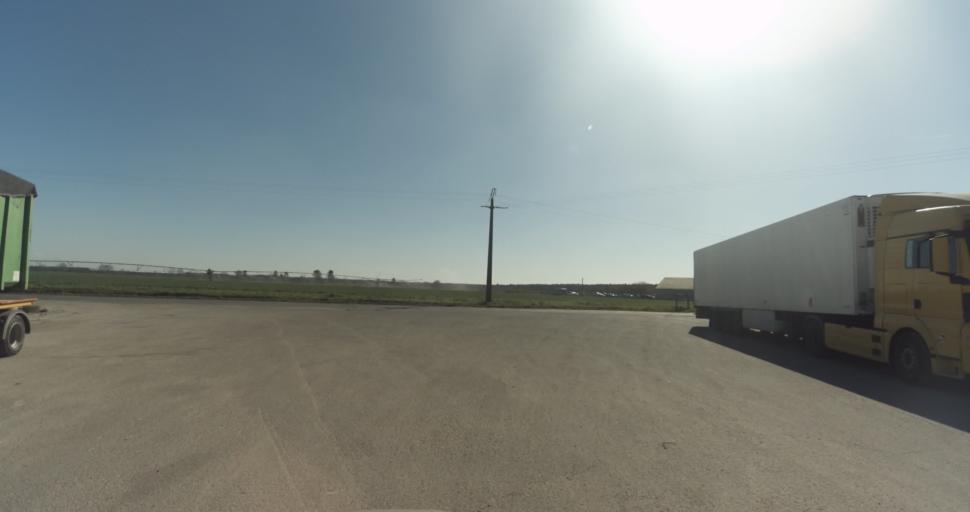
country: FR
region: Aquitaine
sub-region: Departement de la Gironde
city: Marcheprime
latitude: 44.7645
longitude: -0.8545
